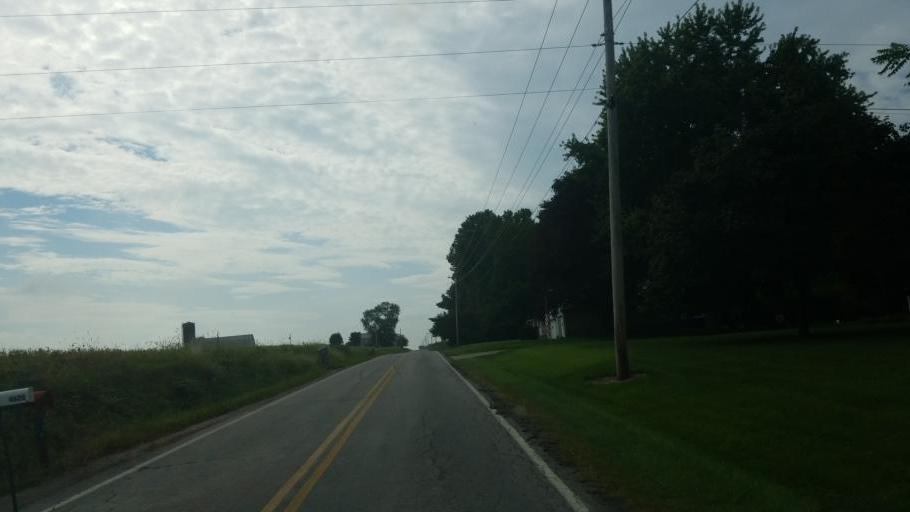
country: US
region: Ohio
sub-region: Wayne County
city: West Salem
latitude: 40.9158
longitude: -82.0196
